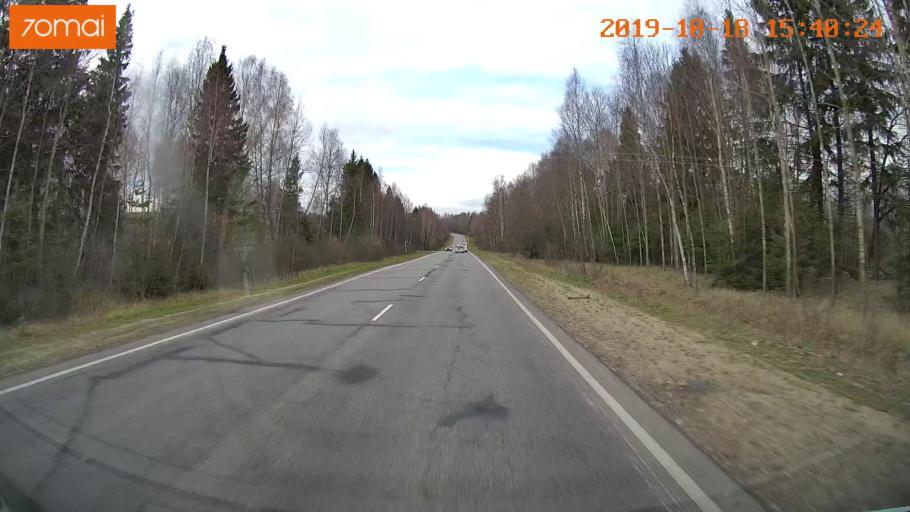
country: RU
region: Vladimir
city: Golovino
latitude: 55.9334
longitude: 40.5939
